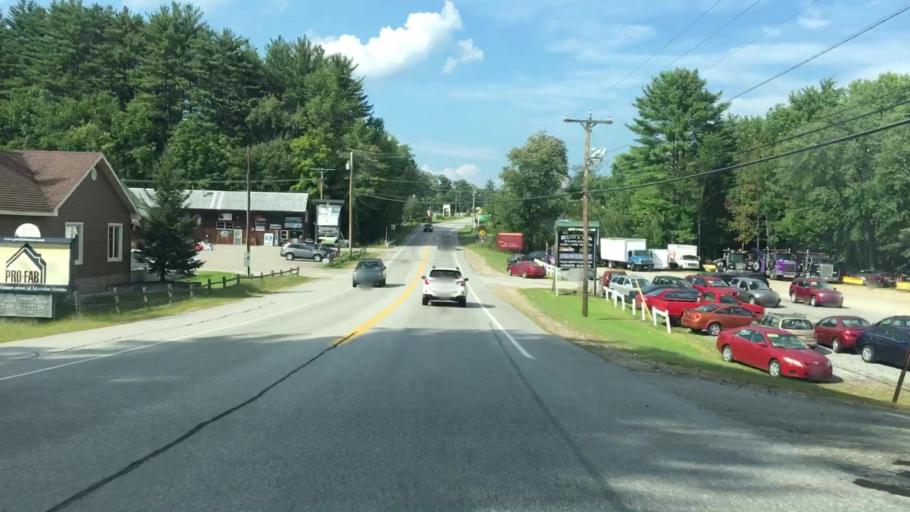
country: US
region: New Hampshire
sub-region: Belknap County
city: Sanbornton
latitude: 43.4729
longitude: -71.5435
